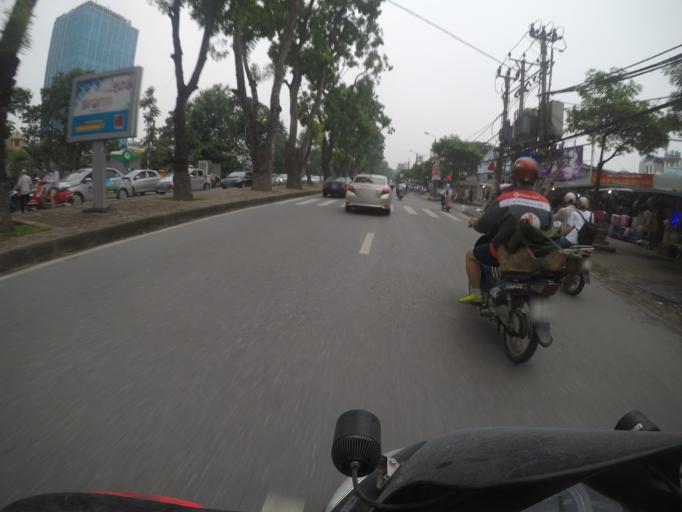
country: VN
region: Ha Noi
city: Thanh Xuan
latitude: 21.0124
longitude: 105.8090
